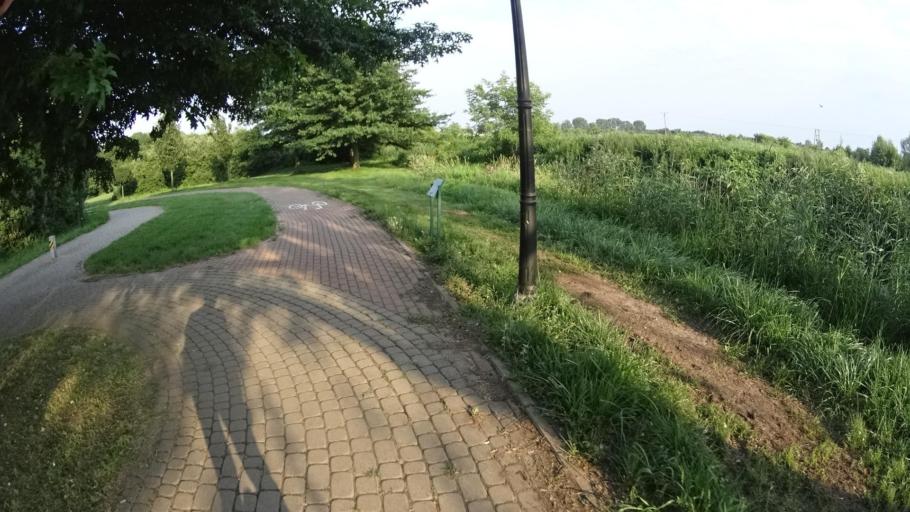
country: PL
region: Masovian Voivodeship
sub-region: Powiat pruszkowski
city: Rybie
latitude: 52.1474
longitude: 20.9282
